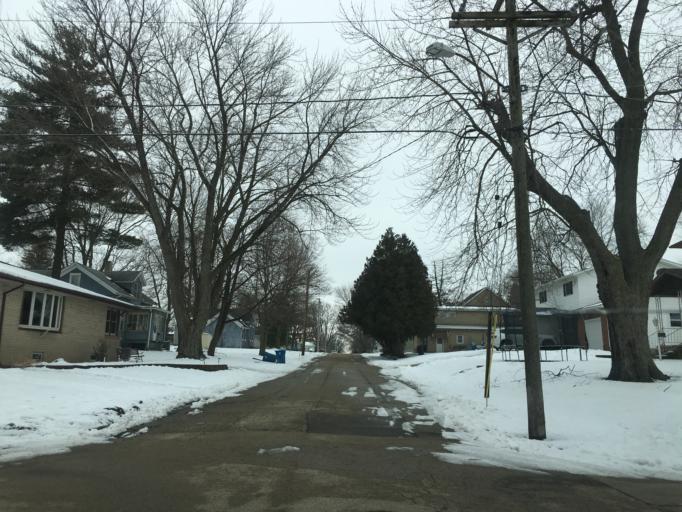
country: US
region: Illinois
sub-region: LaSalle County
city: Peru
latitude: 41.3341
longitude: -89.1279
